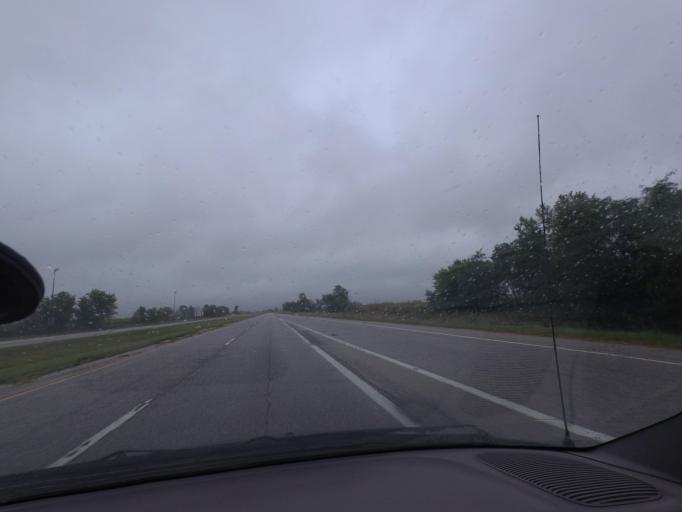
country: US
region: Illinois
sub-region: Pike County
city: Pittsfield
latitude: 39.6709
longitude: -90.8340
